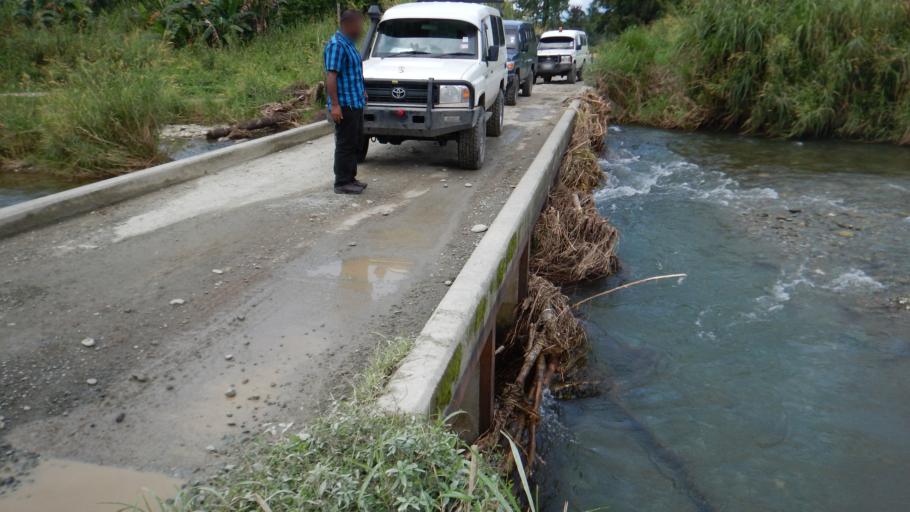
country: PG
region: Northern Province
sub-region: Sohe
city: Kokoda
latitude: -8.9175
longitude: 147.9361
